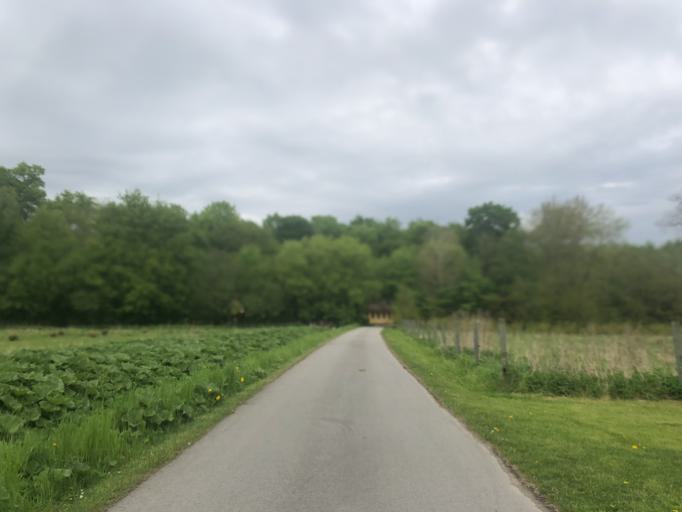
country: DK
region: Zealand
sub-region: Koge Kommune
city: Bjaeverskov
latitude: 55.4321
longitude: 12.0813
